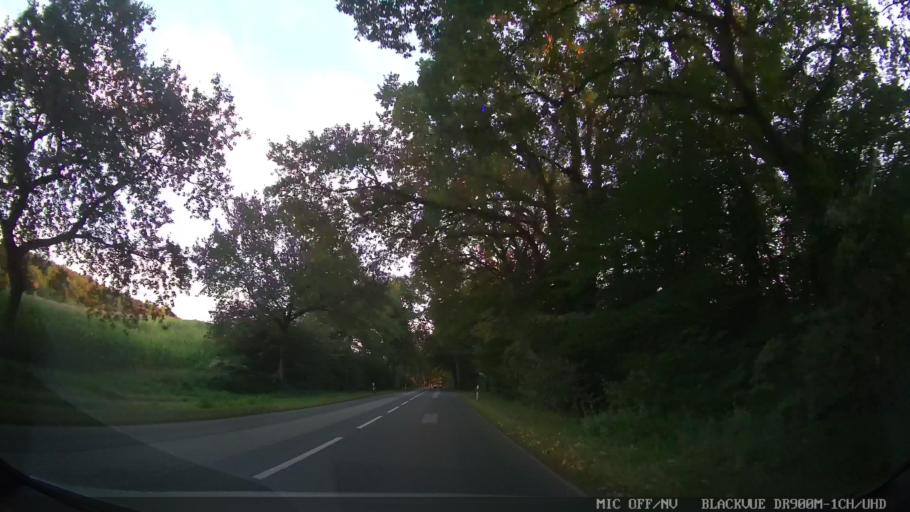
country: DE
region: Schleswig-Holstein
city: Susel
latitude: 54.0207
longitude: 10.6849
